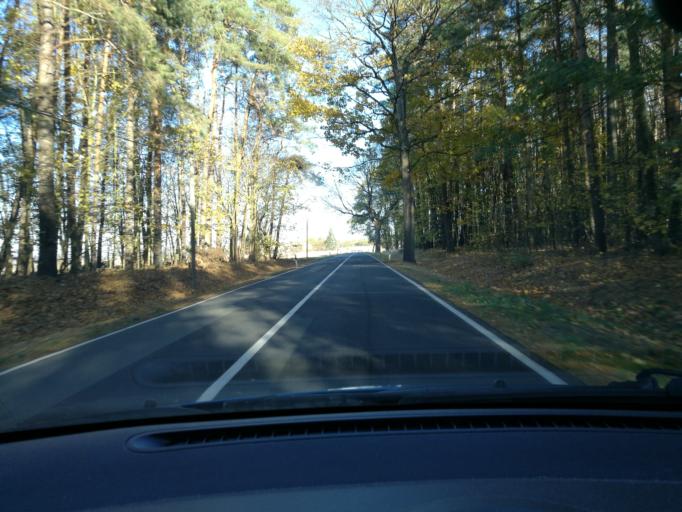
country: DE
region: Brandenburg
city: Lanz
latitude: 53.1432
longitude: 11.5694
